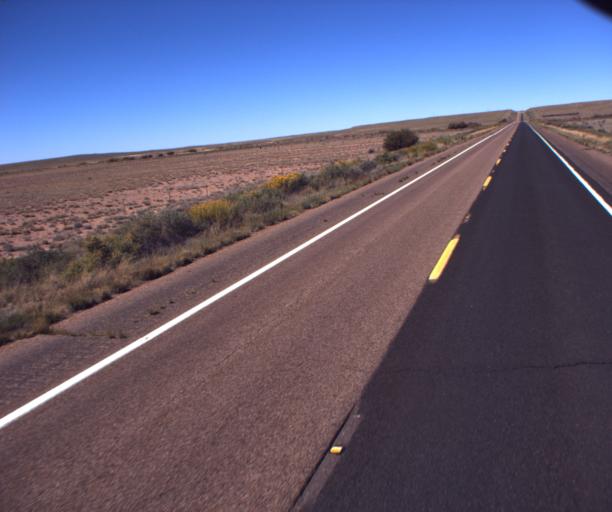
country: US
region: Arizona
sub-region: Navajo County
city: Snowflake
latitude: 34.7407
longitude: -109.7921
